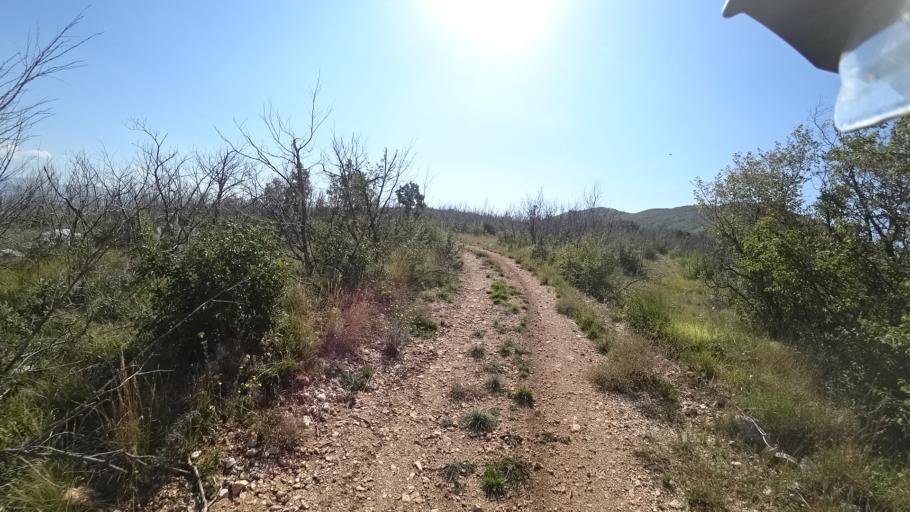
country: HR
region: Sibensko-Kniniska
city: Drnis
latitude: 43.9437
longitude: 16.1537
